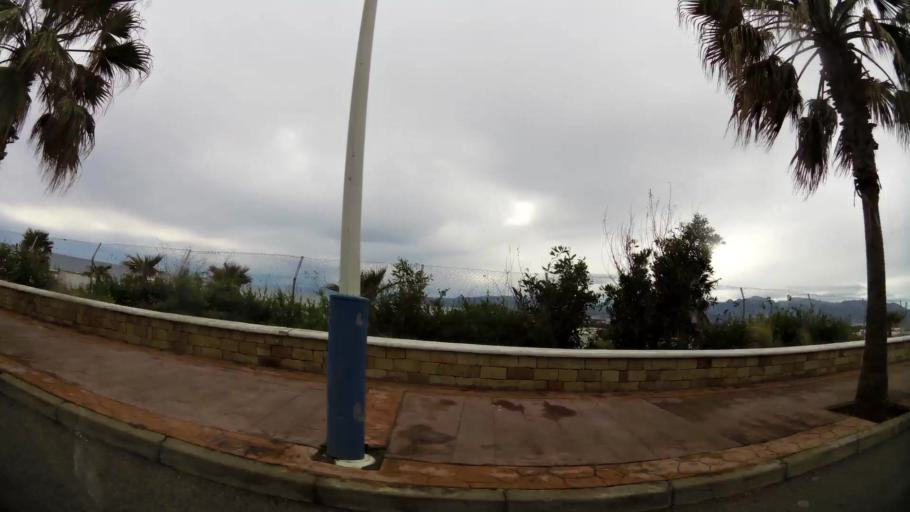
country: MA
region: Tanger-Tetouan
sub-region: Tetouan
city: Martil
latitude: 35.6656
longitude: -5.2885
